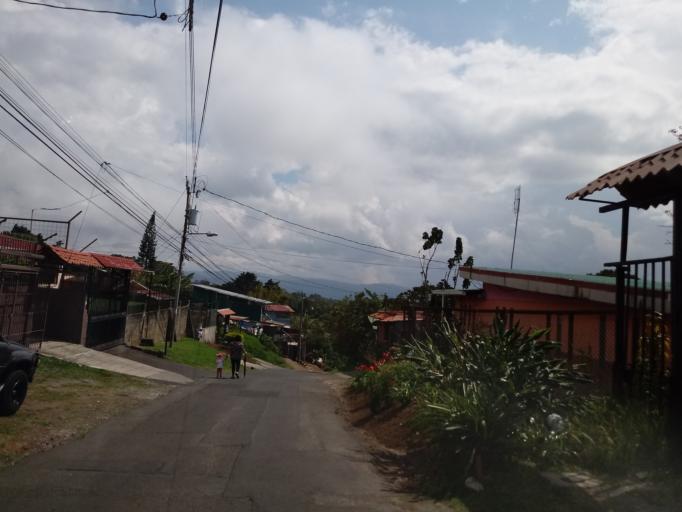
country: CR
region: Heredia
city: Angeles
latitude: 10.0257
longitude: -84.0318
